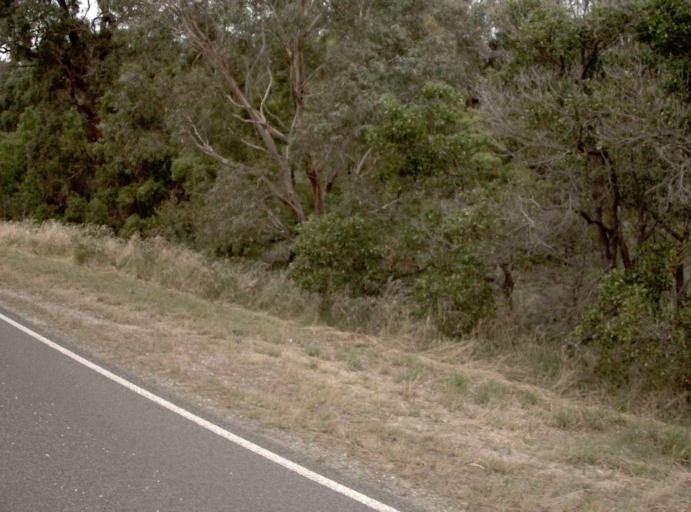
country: AU
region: Victoria
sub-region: Wellington
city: Sale
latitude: -38.1937
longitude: 147.2883
